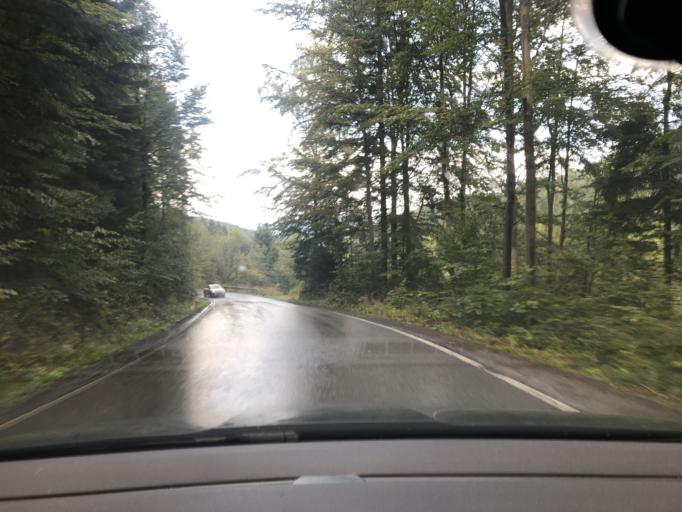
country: PL
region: Lesser Poland Voivodeship
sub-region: Powiat suski
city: Stryszawa
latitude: 49.6912
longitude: 19.5533
